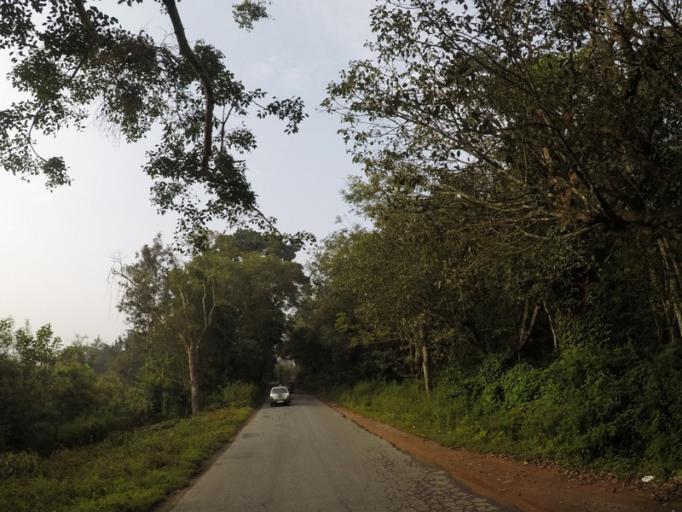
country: IN
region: Karnataka
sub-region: Chikmagalur
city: Chikmagalur
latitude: 13.2619
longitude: 75.6749
